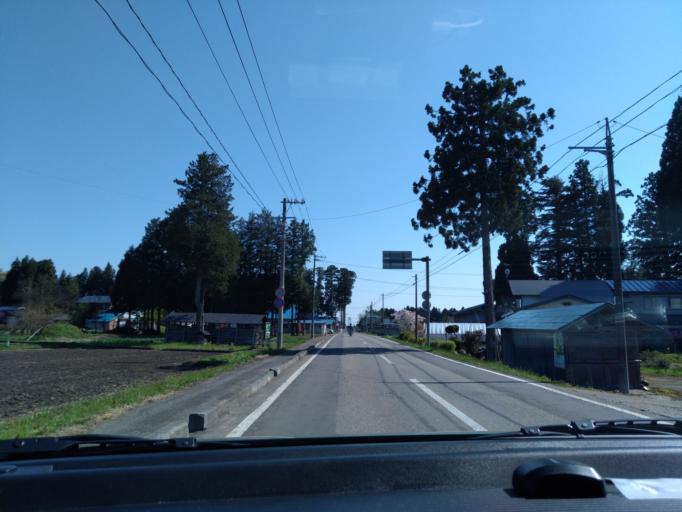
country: JP
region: Akita
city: Kakunodatemachi
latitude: 39.5528
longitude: 140.5860
